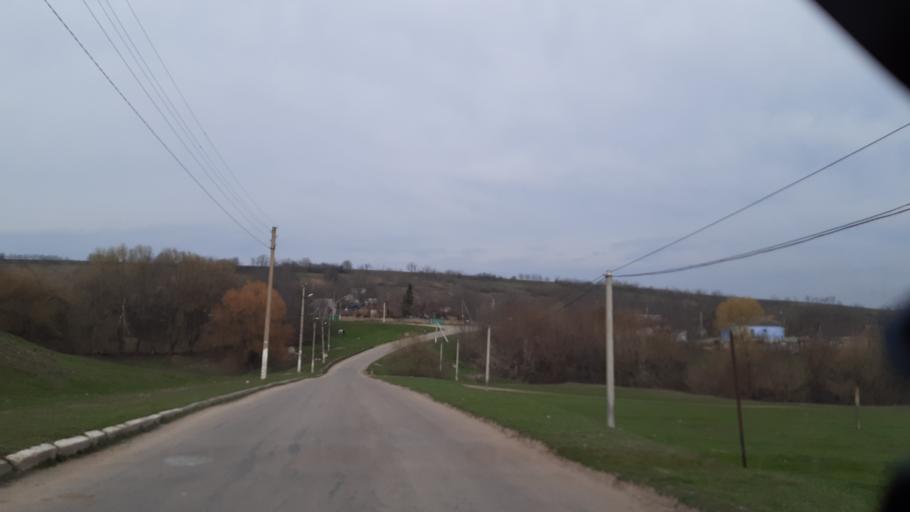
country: MD
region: Soldanesti
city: Soldanesti
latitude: 47.6845
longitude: 28.7757
